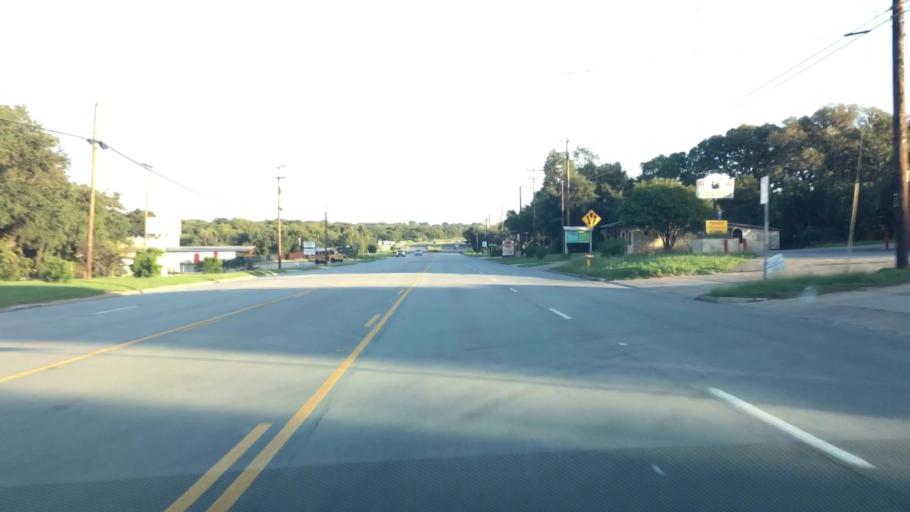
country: US
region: Texas
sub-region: Blanco County
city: Johnson City
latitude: 30.2688
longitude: -98.3981
